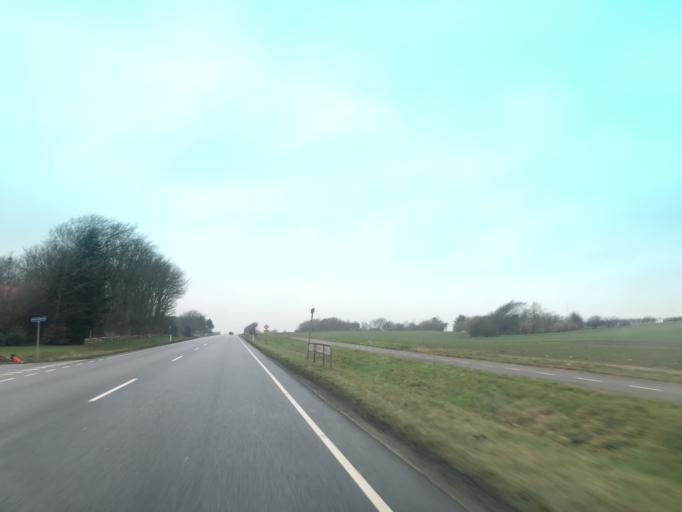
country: DK
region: Central Jutland
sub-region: Struer Kommune
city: Struer
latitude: 56.5272
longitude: 8.5678
